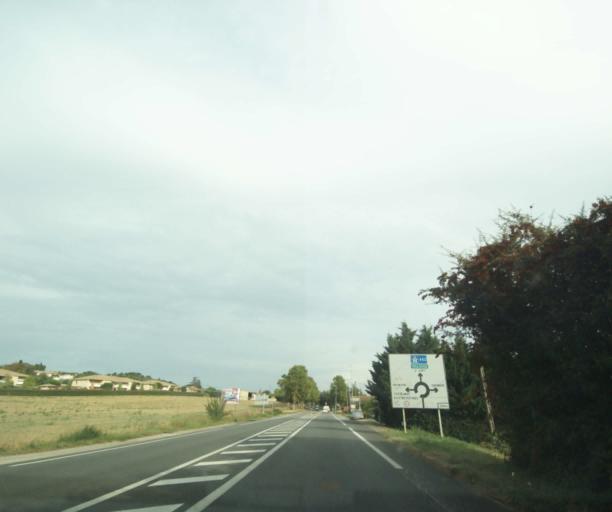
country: FR
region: Midi-Pyrenees
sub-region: Departement de la Haute-Garonne
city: Castelnau-d'Estretefonds
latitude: 43.7904
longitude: 1.3416
